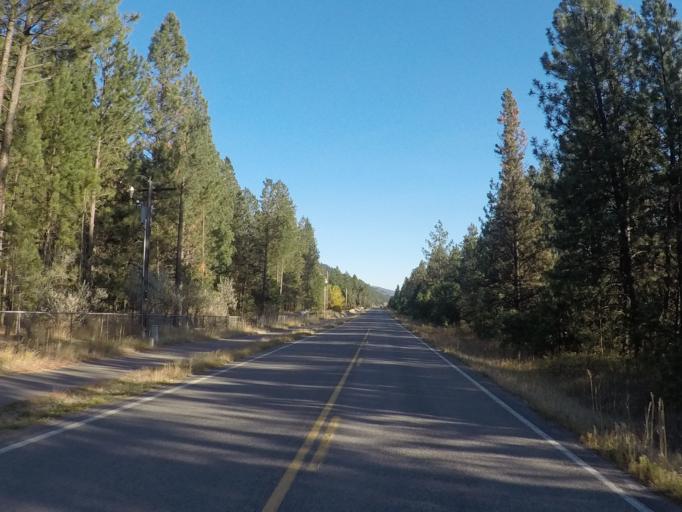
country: US
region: Montana
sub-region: Missoula County
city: Bonner-West Riverside
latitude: 46.8422
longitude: -113.8377
